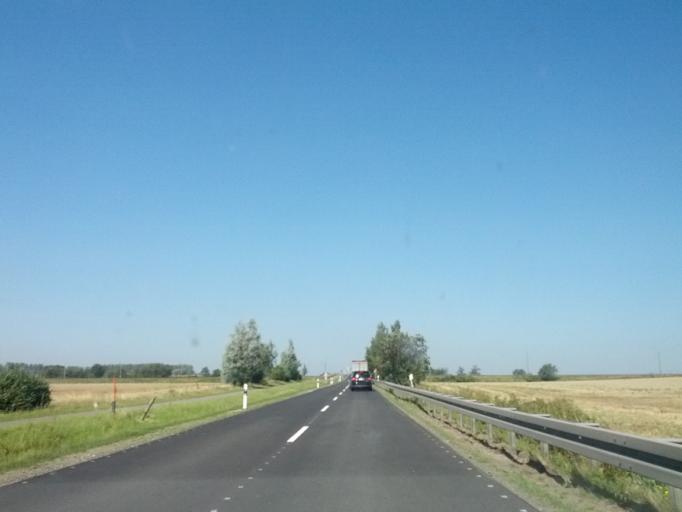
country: DE
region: Mecklenburg-Vorpommern
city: Sagard
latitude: 54.5071
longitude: 13.5420
